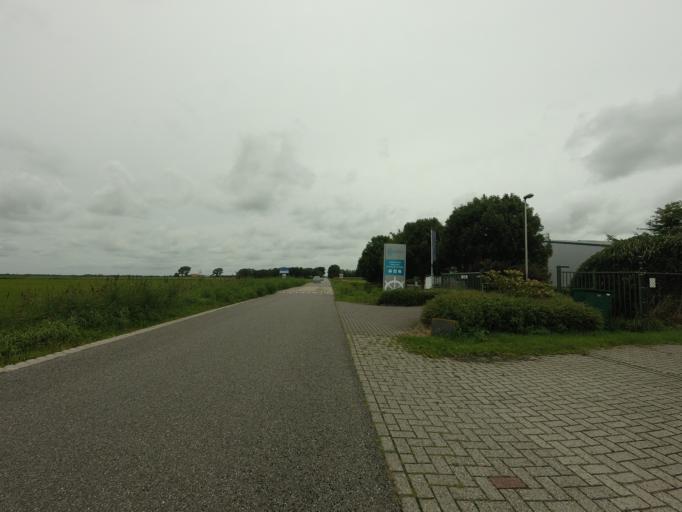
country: NL
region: Overijssel
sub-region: Gemeente Steenwijkerland
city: Oldemarkt
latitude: 52.8092
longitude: 5.9132
